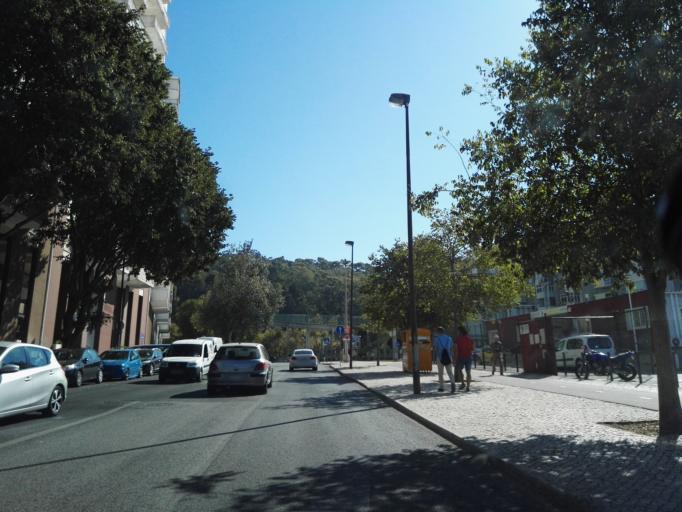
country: PT
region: Lisbon
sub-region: Odivelas
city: Pontinha
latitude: 38.7464
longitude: -9.1898
